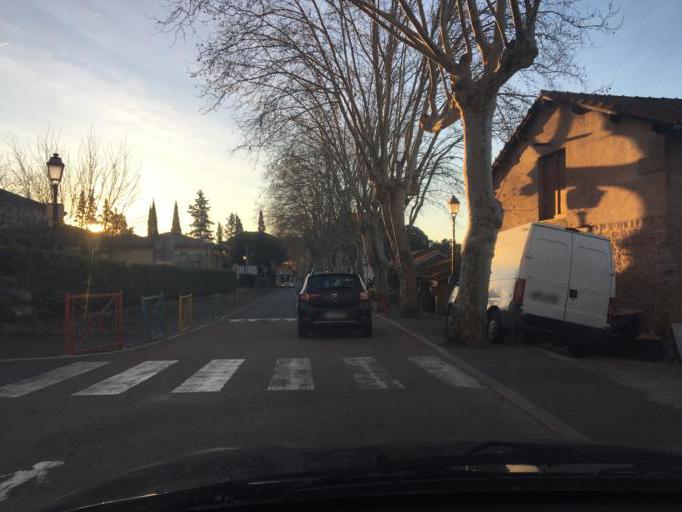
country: FR
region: Provence-Alpes-Cote d'Azur
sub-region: Departement du Var
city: Taradeau
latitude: 43.4540
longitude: 6.4276
